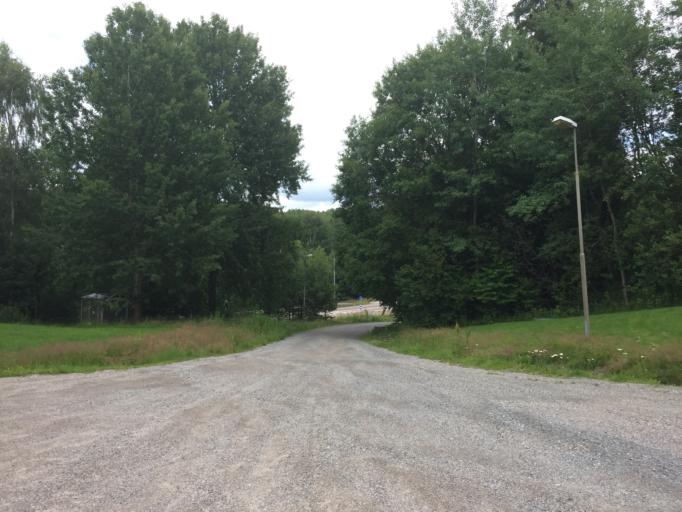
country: SE
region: Stockholm
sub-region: Botkyrka Kommun
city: Tumba
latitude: 59.1983
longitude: 17.8588
